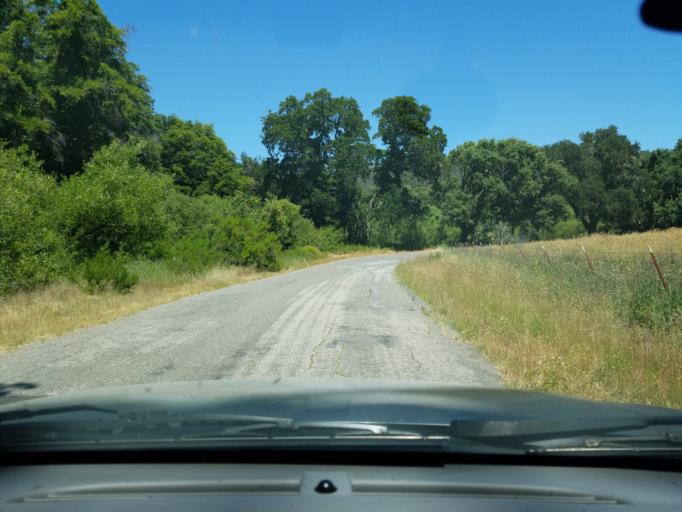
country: US
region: California
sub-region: Monterey County
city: Gonzales
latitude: 36.3508
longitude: -121.5432
